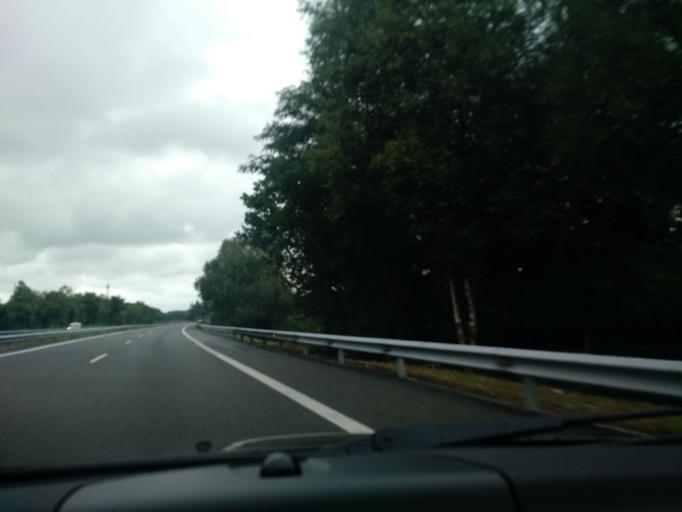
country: ES
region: Galicia
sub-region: Provincia da Coruna
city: Oroso
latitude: 43.0174
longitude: -8.4138
